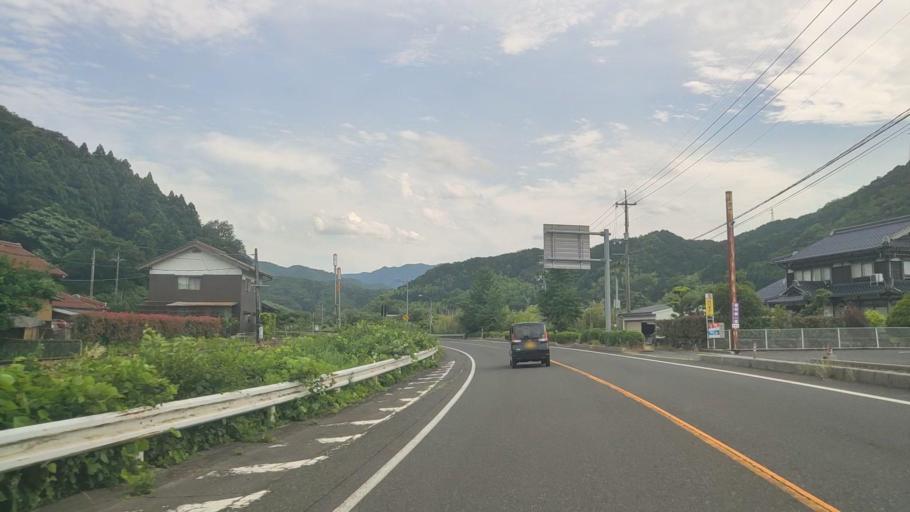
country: JP
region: Tottori
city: Tottori
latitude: 35.3520
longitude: 134.2042
